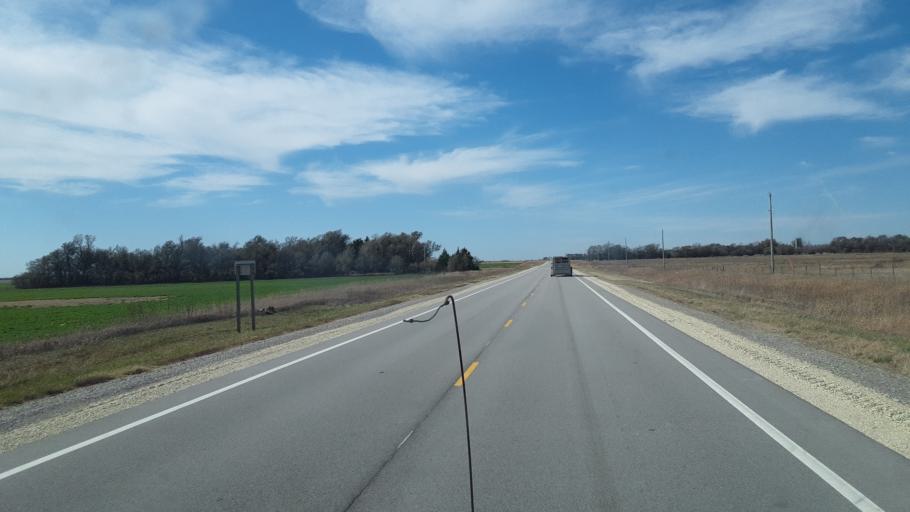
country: US
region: Kansas
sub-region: Marion County
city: Hillsboro
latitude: 38.3771
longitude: -97.3905
